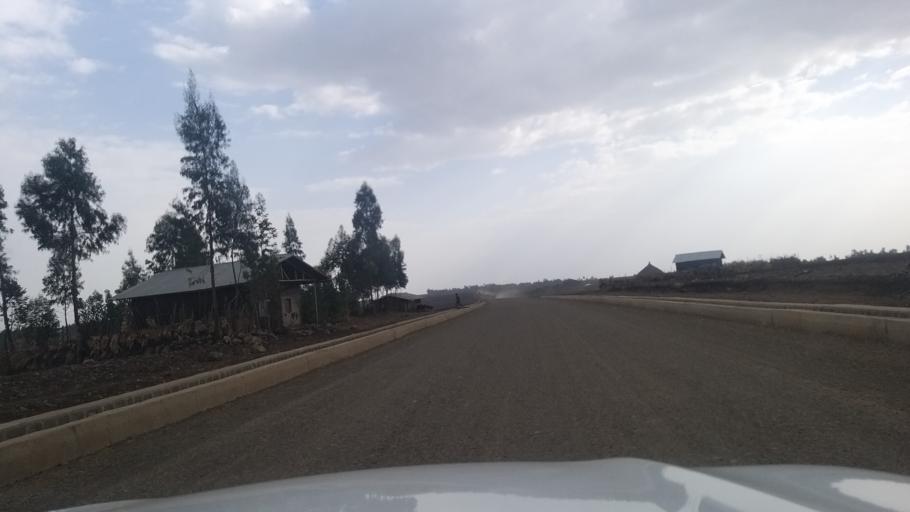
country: ET
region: Amhara
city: Were Ilu
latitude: 10.4472
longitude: 39.1999
